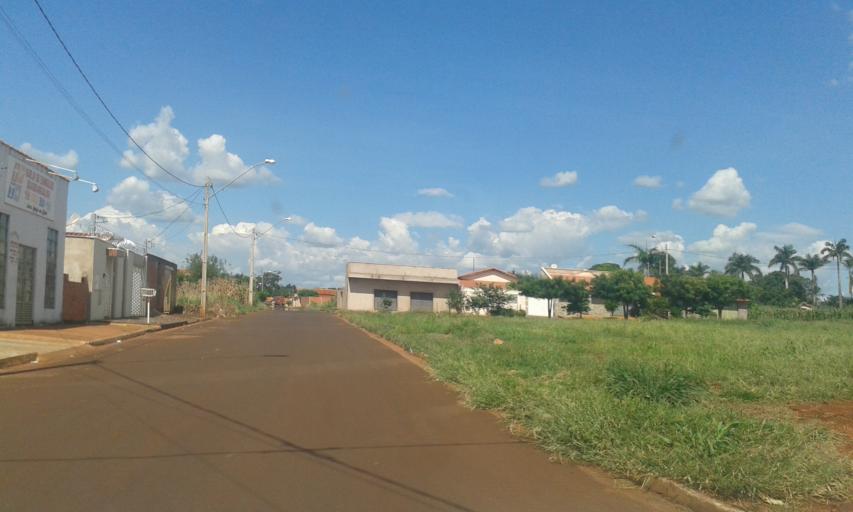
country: BR
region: Minas Gerais
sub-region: Capinopolis
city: Capinopolis
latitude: -18.6886
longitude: -49.5761
